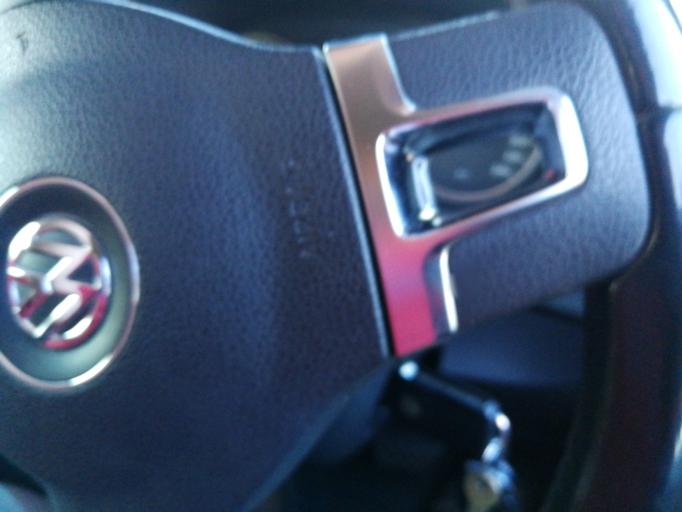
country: ZA
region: Limpopo
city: Thulamahashi
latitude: -25.0232
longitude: 31.3338
